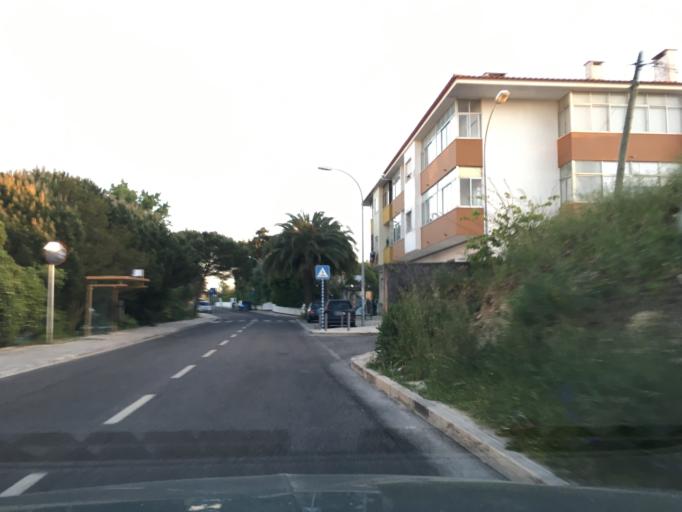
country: PT
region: Lisbon
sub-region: Oeiras
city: Terrugem
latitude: 38.7053
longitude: -9.2880
